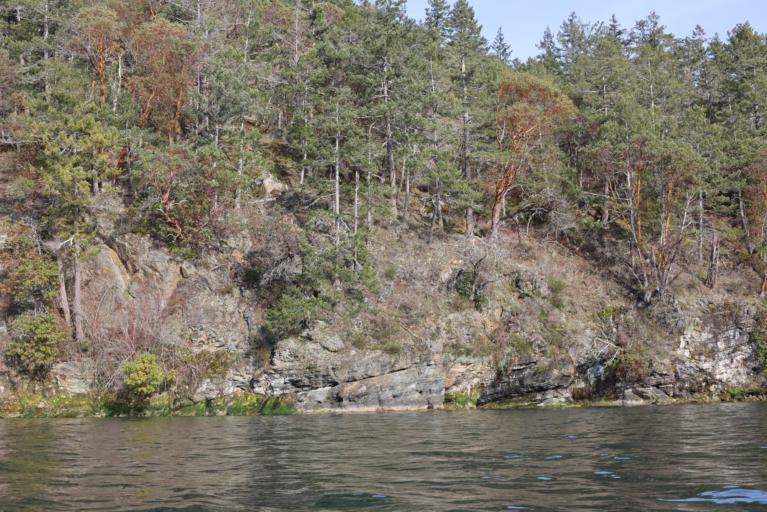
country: CA
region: British Columbia
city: Duncan
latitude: 48.7554
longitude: -123.6037
